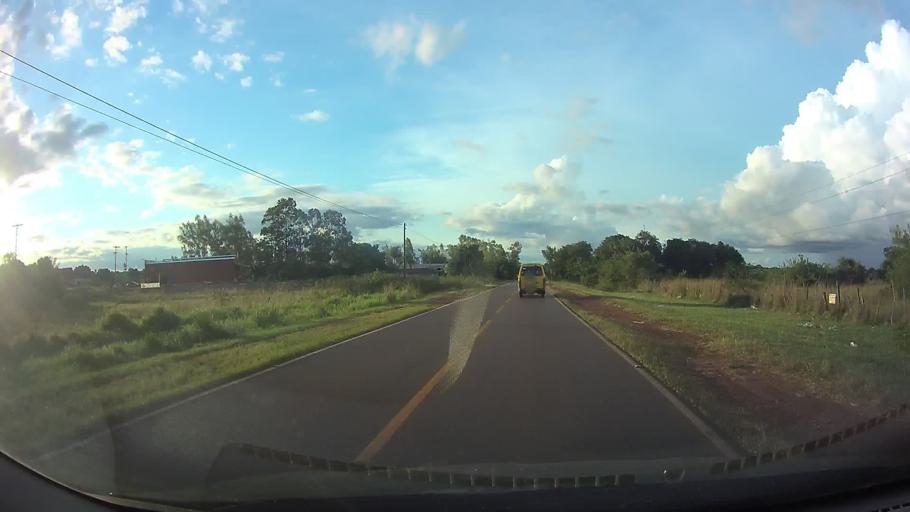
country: PY
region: Paraguari
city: Carapegua
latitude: -25.7769
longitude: -57.2275
